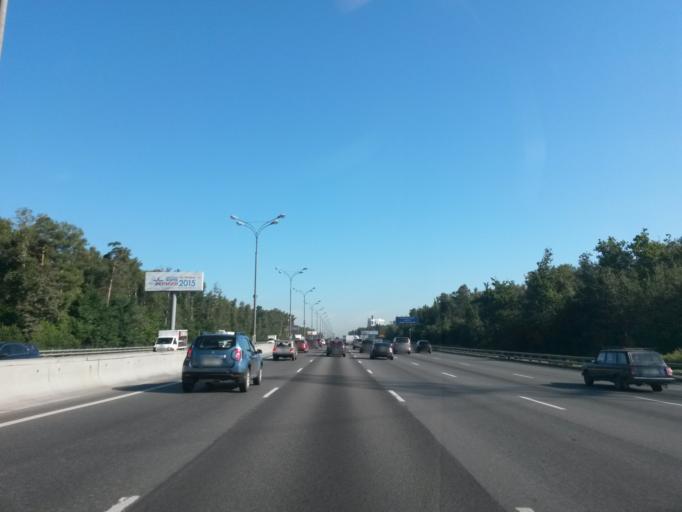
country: RU
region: Moscow
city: Ivanovskoye
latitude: 55.7888
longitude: 37.8415
